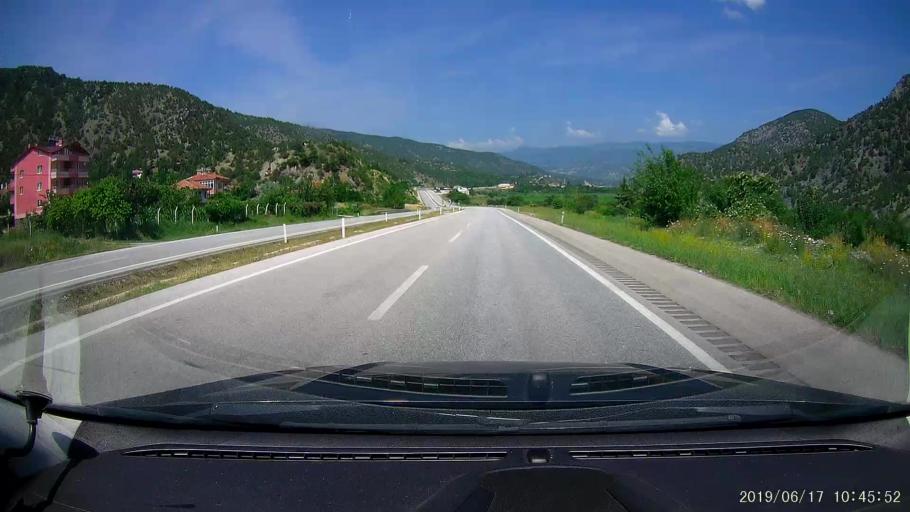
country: TR
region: Corum
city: Hacihamza
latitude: 41.0640
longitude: 34.4765
